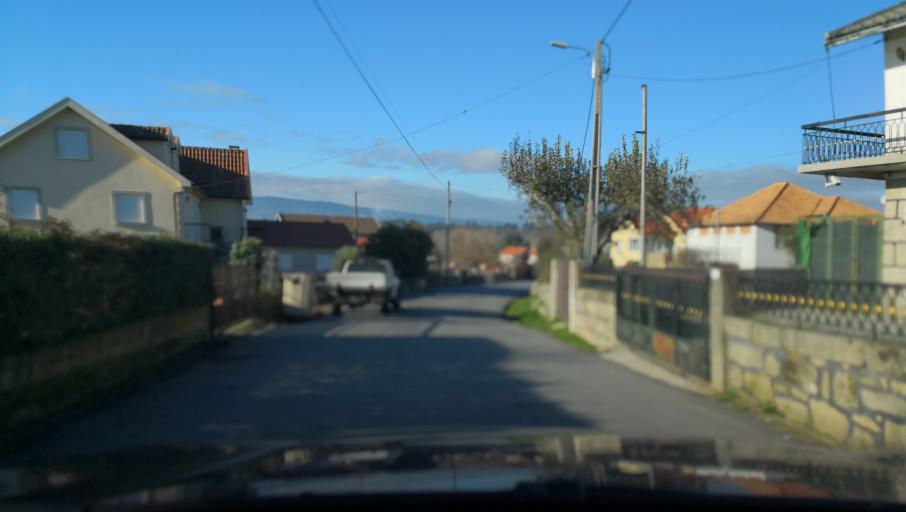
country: PT
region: Vila Real
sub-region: Vila Real
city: Vila Real
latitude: 41.3377
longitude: -7.6633
